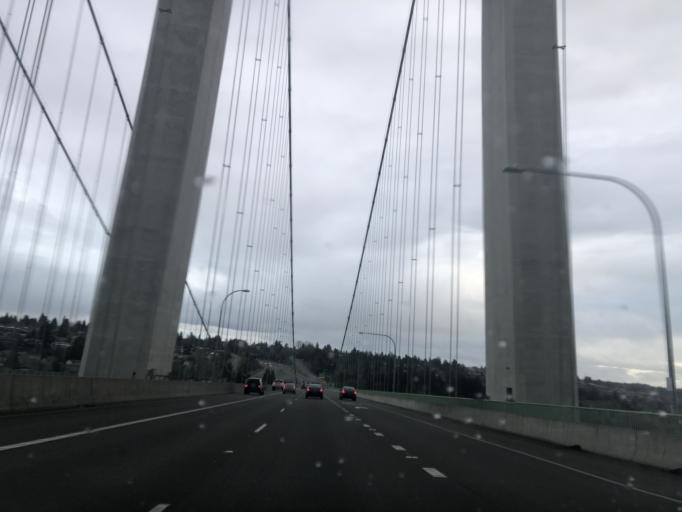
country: US
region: Washington
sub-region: Pierce County
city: University Place
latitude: 47.2651
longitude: -122.5471
